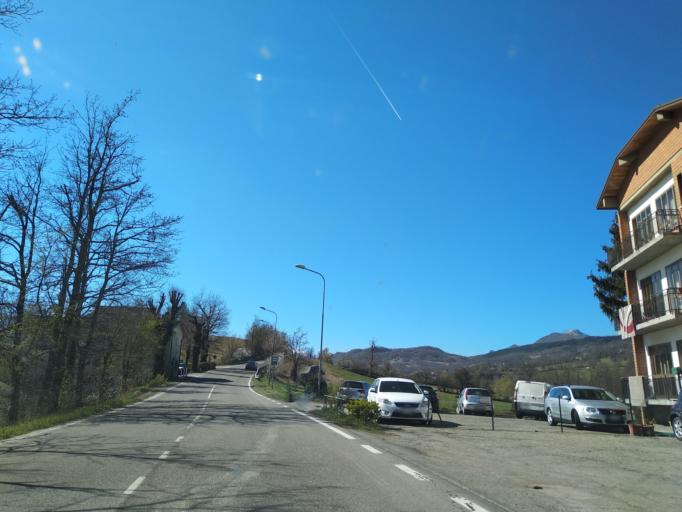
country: IT
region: Emilia-Romagna
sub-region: Provincia di Reggio Emilia
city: Castelnovo ne'Monti
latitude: 44.4248
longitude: 10.3809
